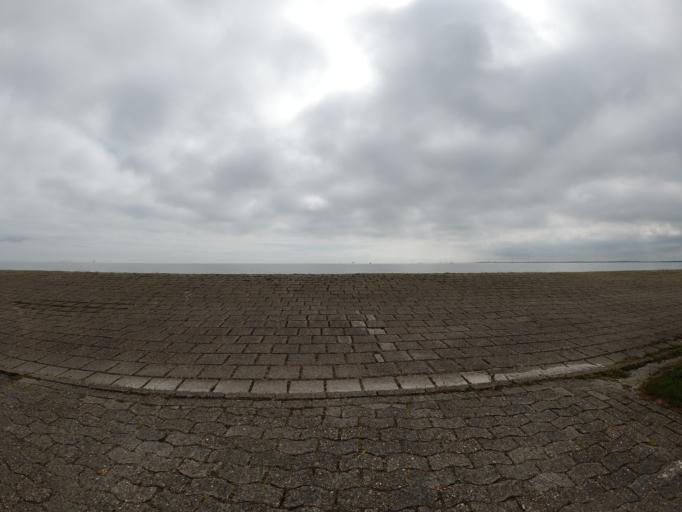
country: DE
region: Lower Saxony
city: Schillig
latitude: 53.6973
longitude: 8.0288
